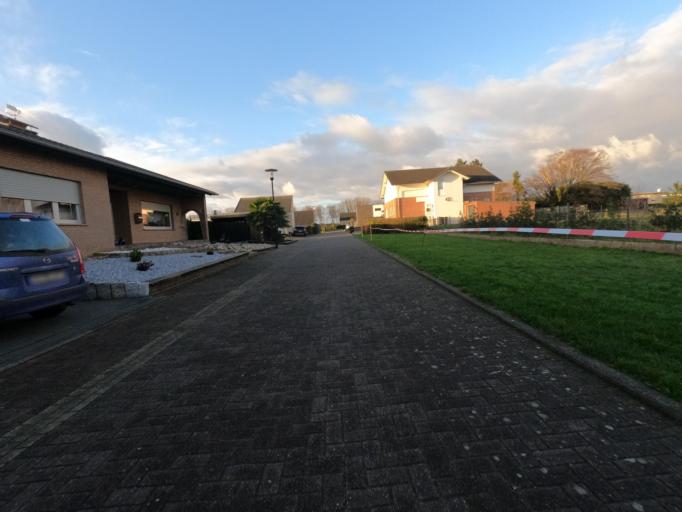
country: DE
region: North Rhine-Westphalia
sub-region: Regierungsbezirk Koln
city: Heinsberg
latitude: 51.0915
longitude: 6.1019
